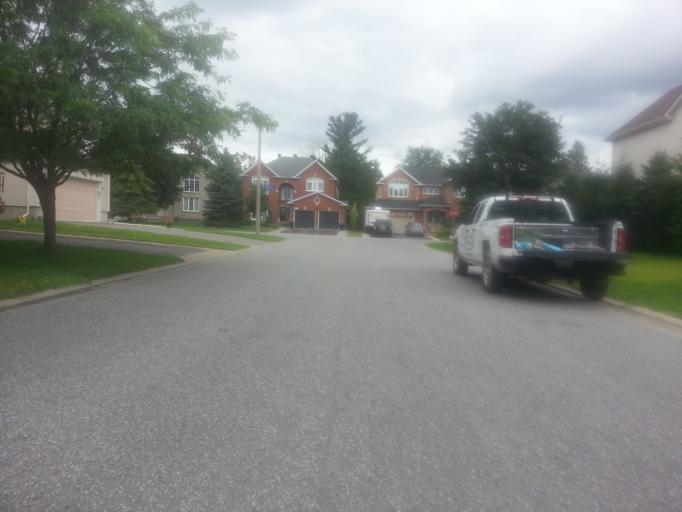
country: CA
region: Ontario
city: Bells Corners
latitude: 45.3265
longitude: -75.9274
